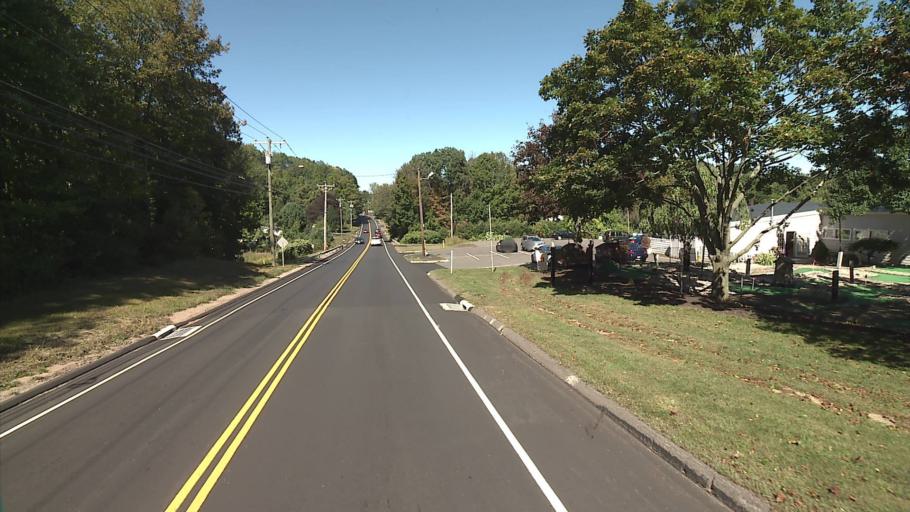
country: US
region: Connecticut
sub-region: New Haven County
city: Prospect
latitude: 41.5223
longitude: -72.9939
